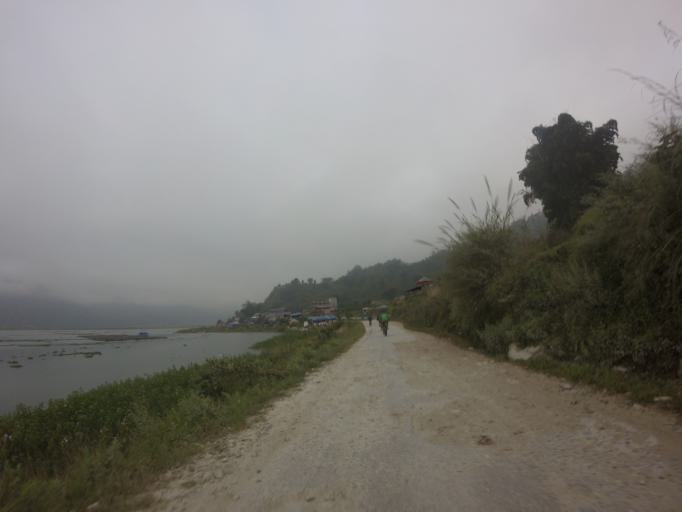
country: NP
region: Western Region
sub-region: Gandaki Zone
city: Pokhara
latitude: 28.2275
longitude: 83.9398
